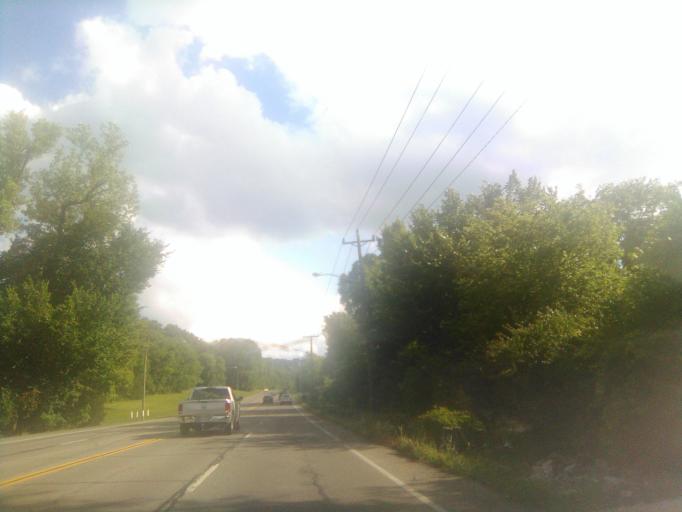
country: US
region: Tennessee
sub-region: Davidson County
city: Belle Meade
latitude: 36.0832
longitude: -86.8833
